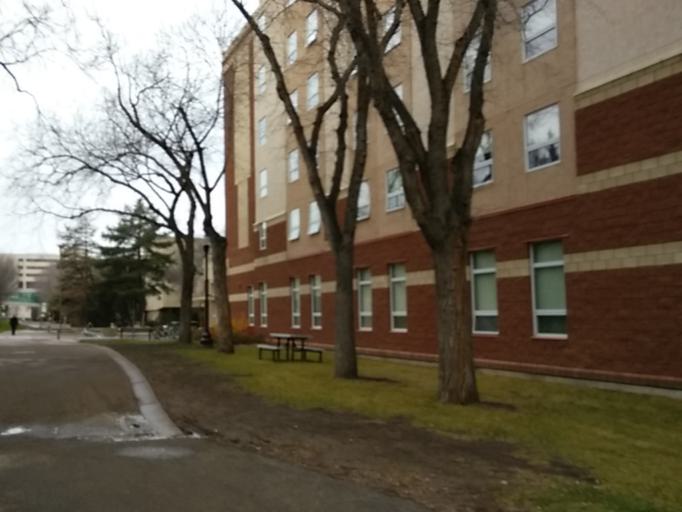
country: CA
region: Alberta
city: Edmonton
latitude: 53.5239
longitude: -113.5169
